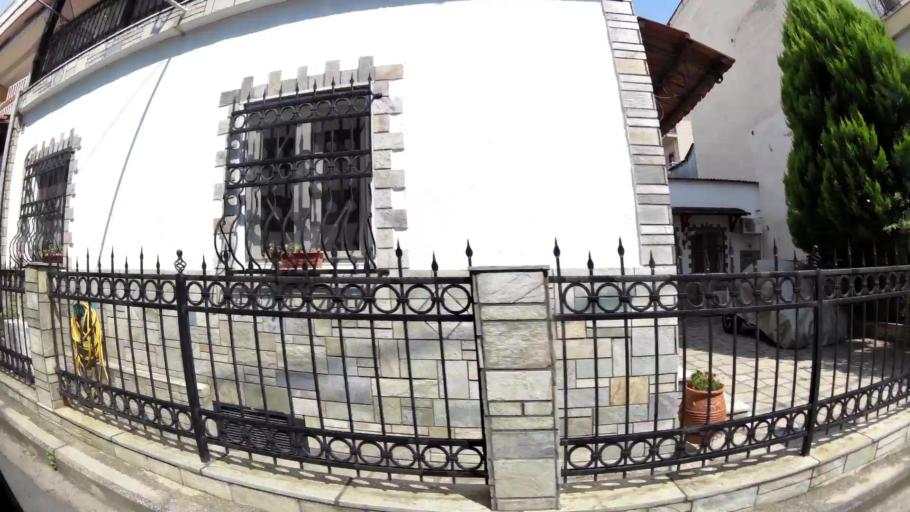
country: GR
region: Central Macedonia
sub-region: Nomos Thessalonikis
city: Polichni
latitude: 40.6650
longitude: 22.9430
